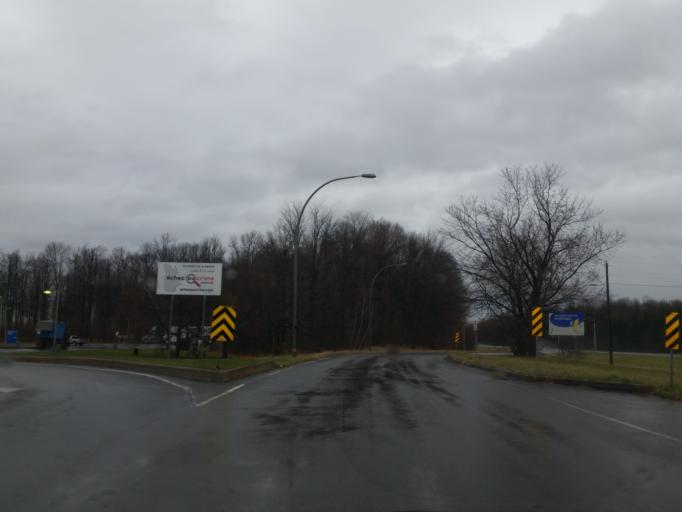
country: CA
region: Quebec
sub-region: Lanaudiere
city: Lavaltrie
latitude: 45.8904
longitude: -73.3488
